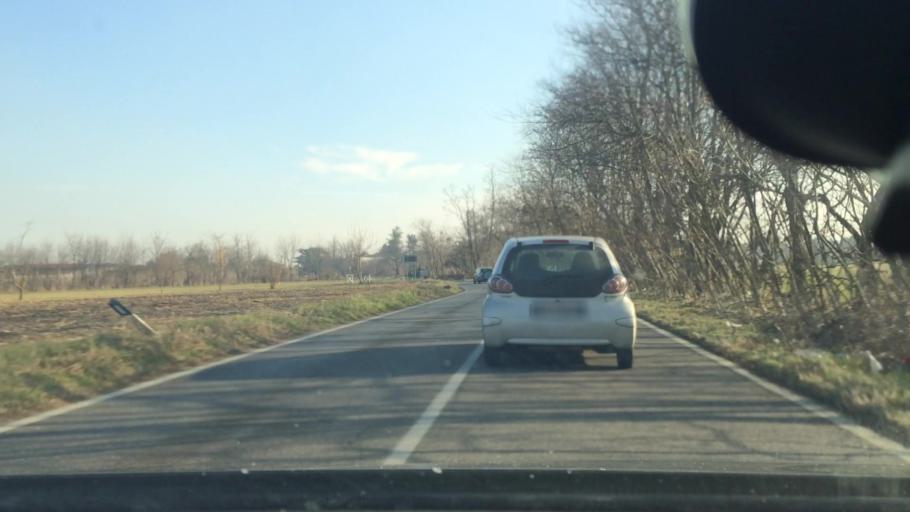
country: IT
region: Lombardy
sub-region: Citta metropolitana di Milano
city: Arluno
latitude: 45.5120
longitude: 8.9242
